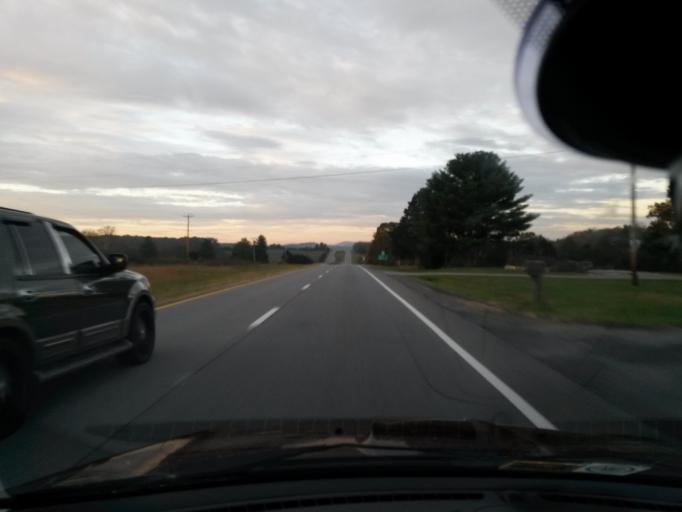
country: US
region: Virginia
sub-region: Botetourt County
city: Fincastle
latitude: 37.5478
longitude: -79.8581
